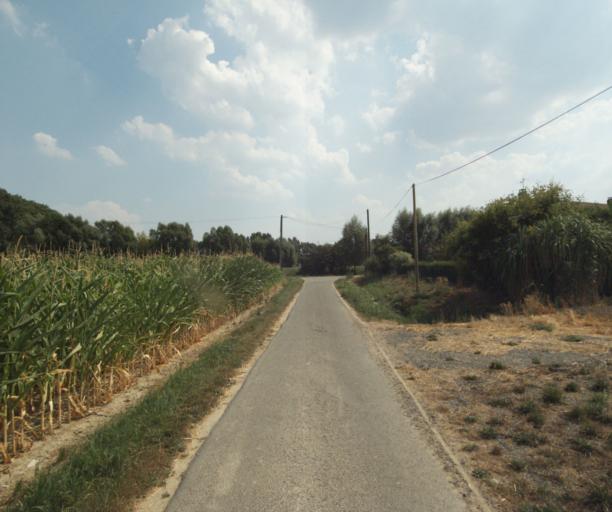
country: FR
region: Nord-Pas-de-Calais
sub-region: Departement du Nord
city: Quesnoy-sur-Deule
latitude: 50.7293
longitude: 2.9979
